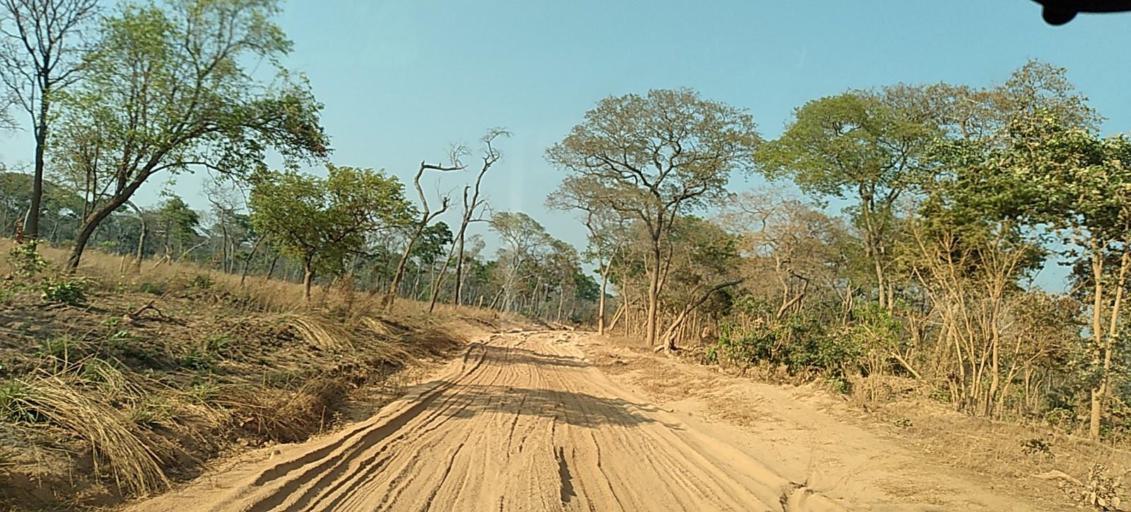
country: ZM
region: North-Western
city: Kasempa
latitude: -13.5718
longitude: 25.9937
